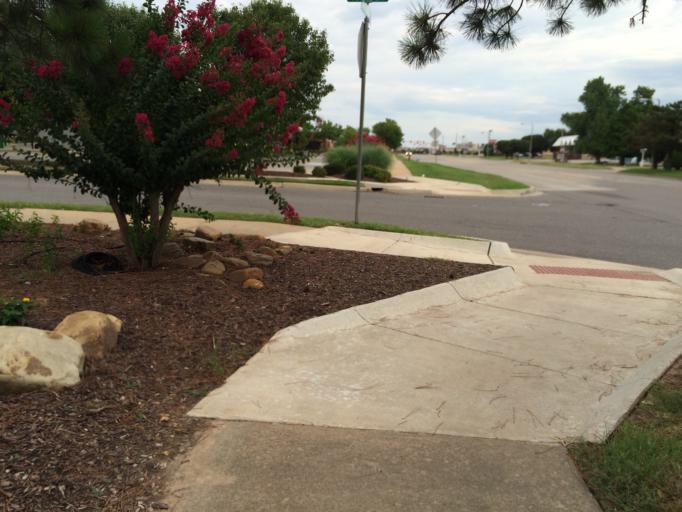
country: US
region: Oklahoma
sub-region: Cleveland County
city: Norman
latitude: 35.2298
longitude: -97.4806
